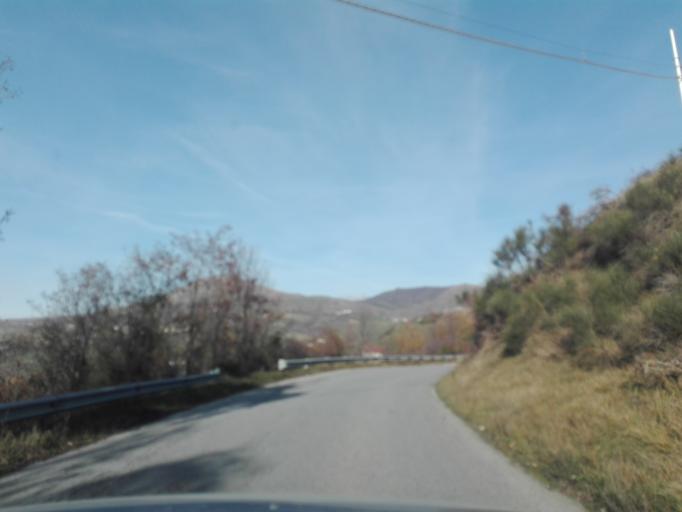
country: IT
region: Molise
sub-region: Provincia di Isernia
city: Agnone
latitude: 41.8228
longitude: 14.3773
